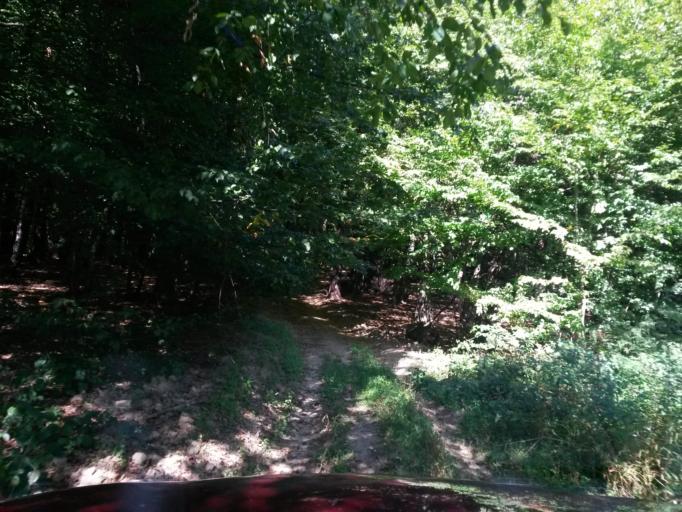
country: SK
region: Presovsky
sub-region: Okres Presov
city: Presov
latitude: 48.9812
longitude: 21.1481
